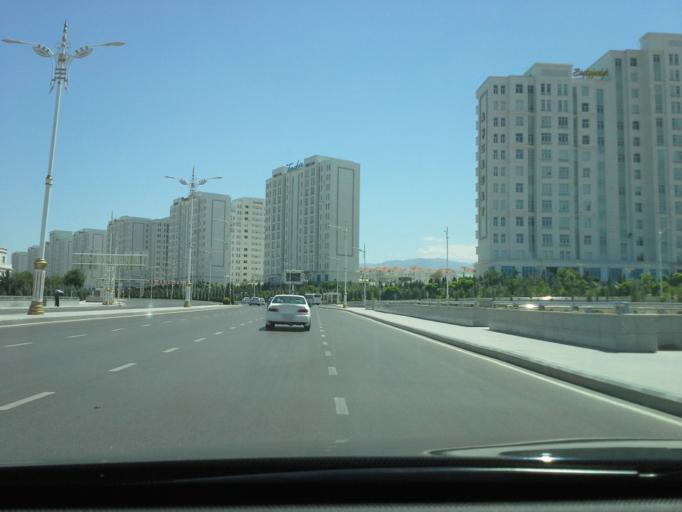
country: TM
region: Ahal
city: Ashgabat
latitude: 37.9401
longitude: 58.3647
